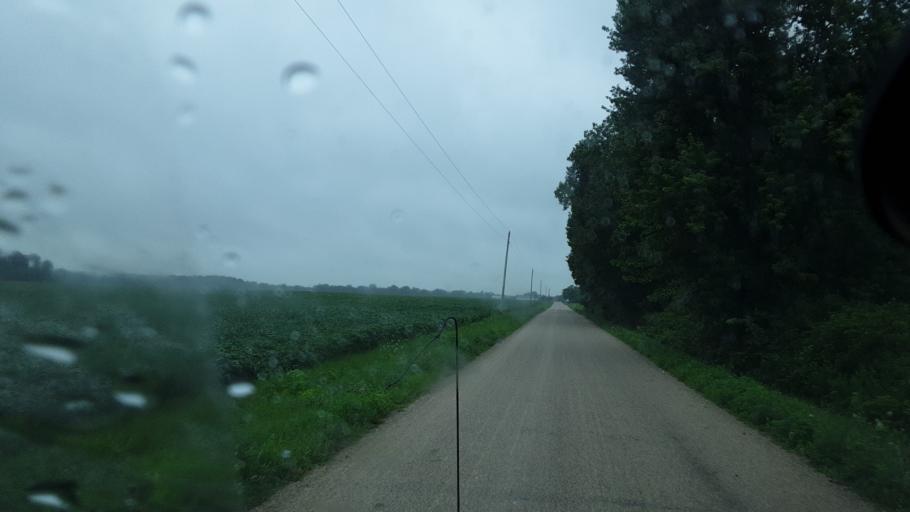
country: US
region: Indiana
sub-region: Adams County
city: Berne
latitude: 40.7037
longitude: -84.8146
